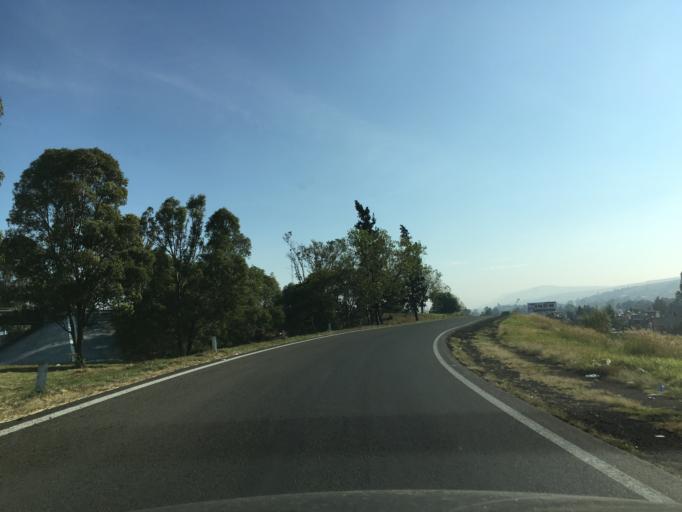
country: MX
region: Michoacan
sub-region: Tarimbaro
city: Conjunto Habitacional el Trebol
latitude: 19.7678
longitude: -101.1588
